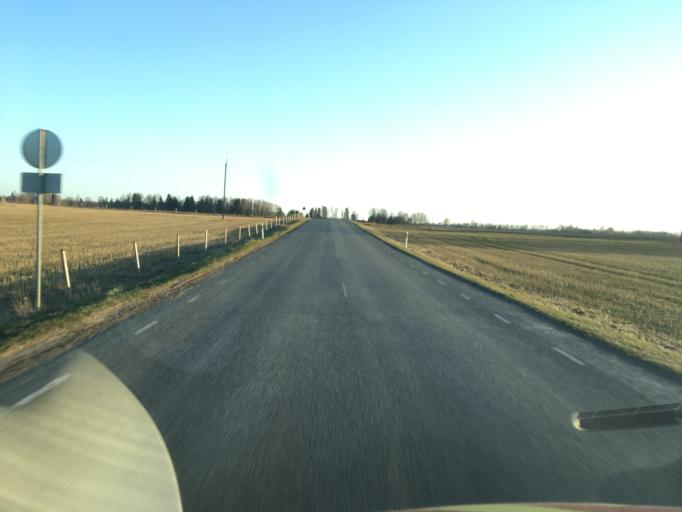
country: EE
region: Raplamaa
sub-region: Kehtna vald
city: Kehtna
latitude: 59.0194
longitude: 24.9249
